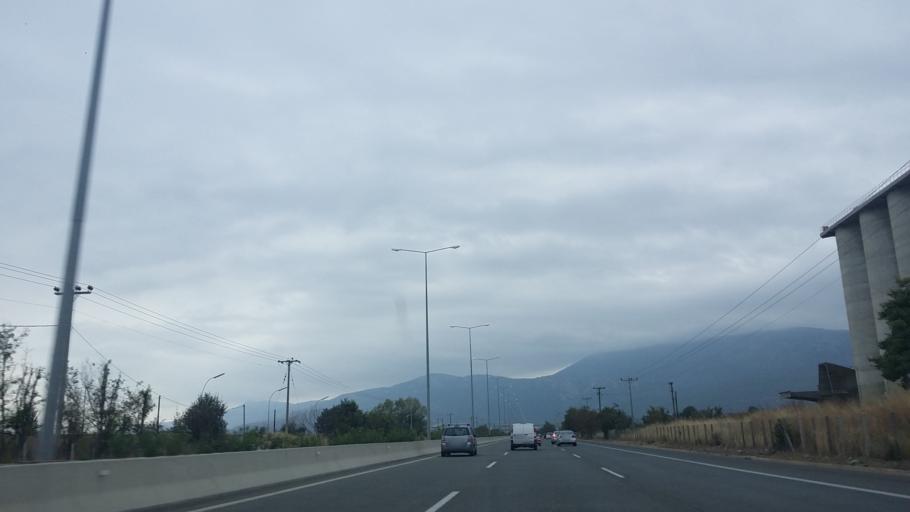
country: GR
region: Attica
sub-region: Nomarchia Anatolikis Attikis
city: Avlonas
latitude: 38.2802
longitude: 23.6858
